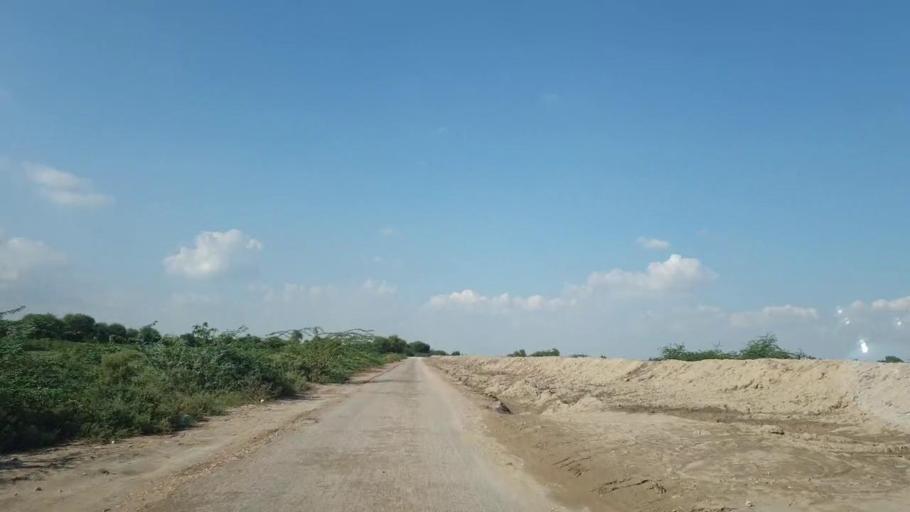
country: PK
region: Sindh
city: Pithoro
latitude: 25.6320
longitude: 69.4358
